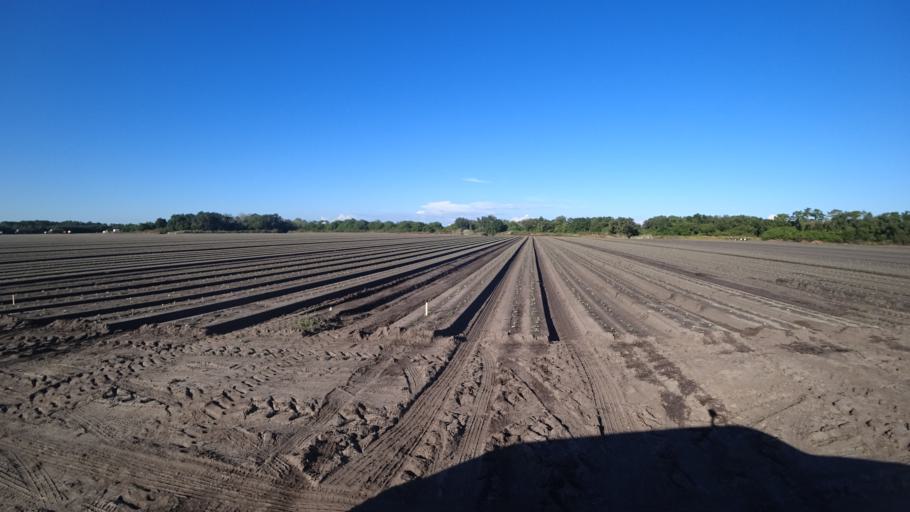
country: US
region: Florida
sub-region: Hillsborough County
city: Ruskin
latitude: 27.6397
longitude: -82.4359
